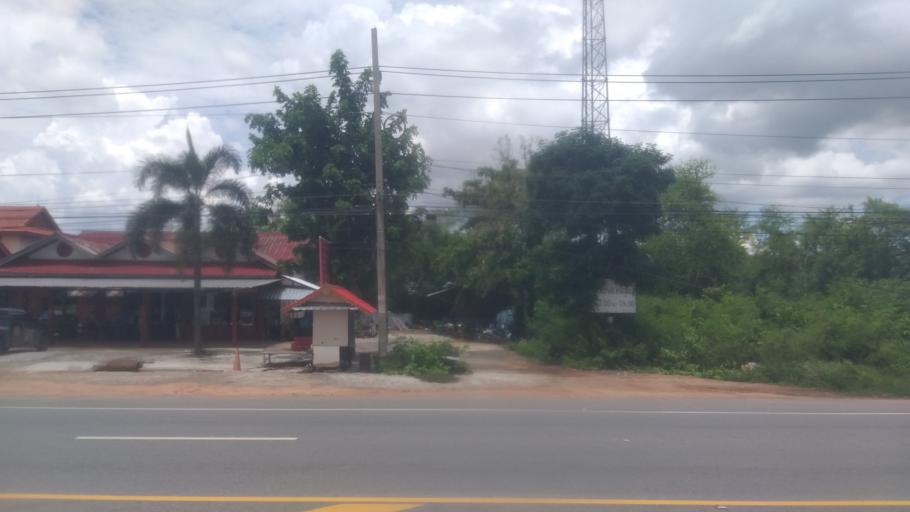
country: TH
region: Nakhon Ratchasima
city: Non Thai
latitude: 15.1127
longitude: 102.1015
